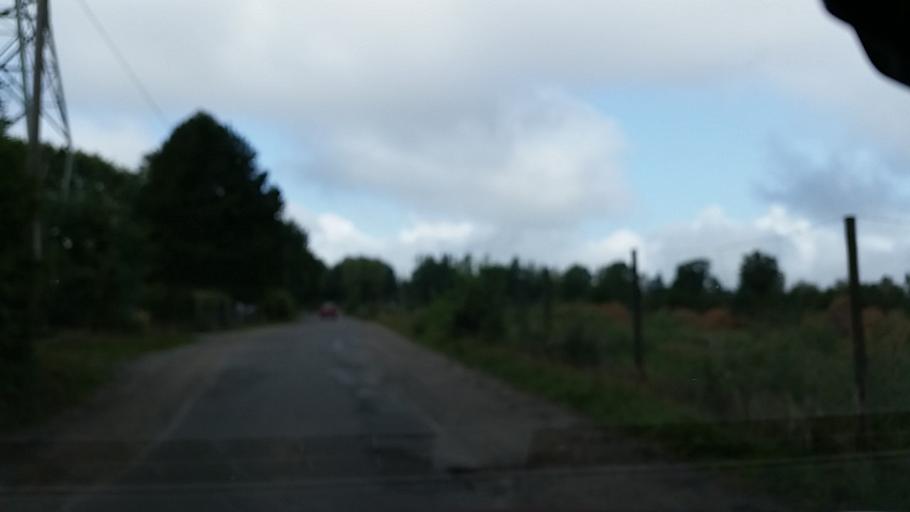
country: DE
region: Schleswig-Holstein
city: Wedel
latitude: 53.6028
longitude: 9.7221
